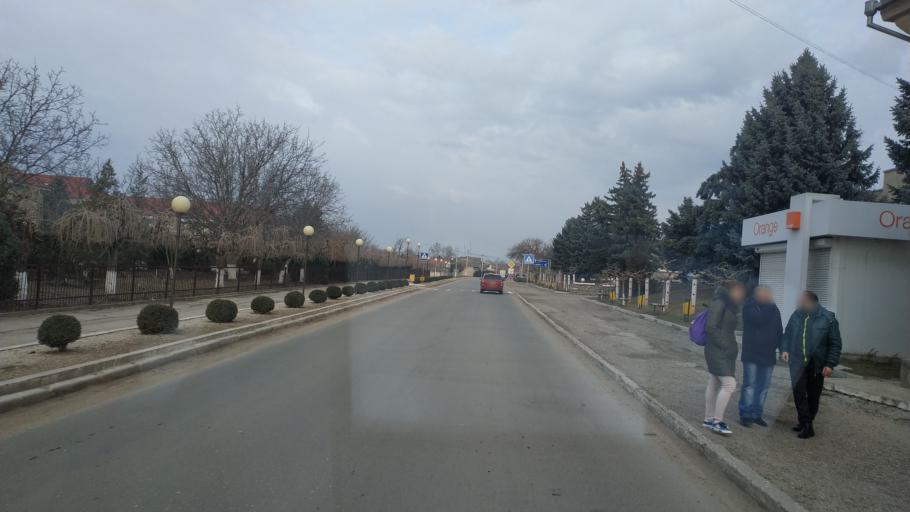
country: MD
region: Chisinau
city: Singera
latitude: 46.9626
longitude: 29.0569
